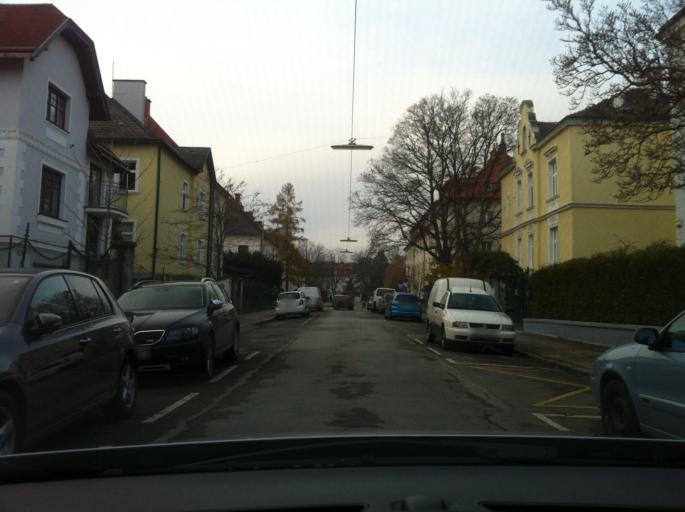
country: AT
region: Lower Austria
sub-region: Politischer Bezirk Modling
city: Perchtoldsdorf
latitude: 48.1956
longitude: 16.2736
